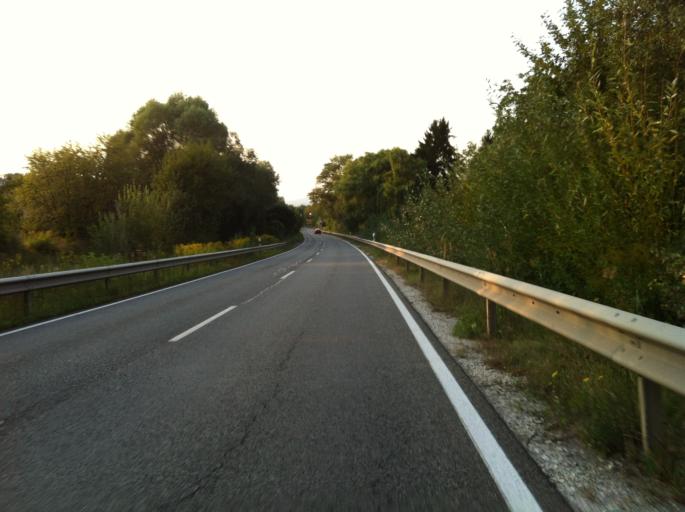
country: DE
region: Rheinland-Pfalz
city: Ingelheim am Rhein
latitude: 49.9572
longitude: 8.0591
